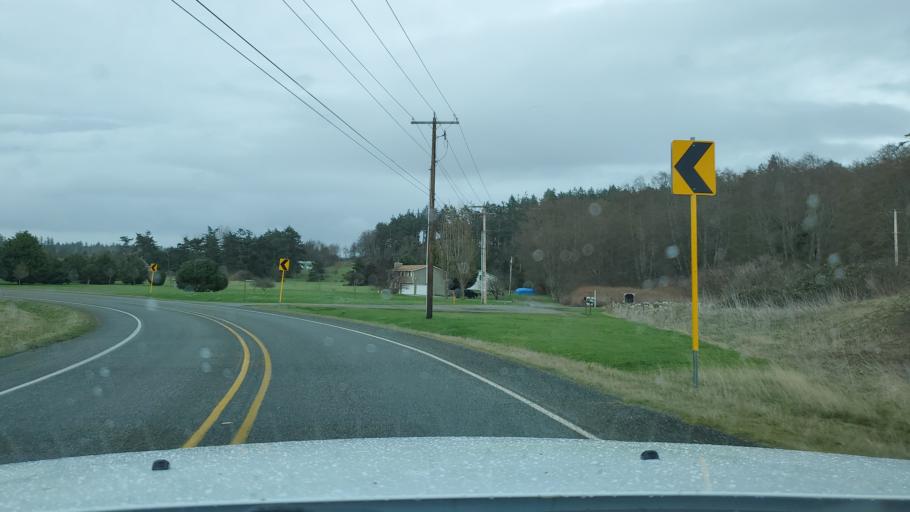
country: US
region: Washington
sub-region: Island County
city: Ault Field
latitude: 48.3078
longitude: -122.7033
